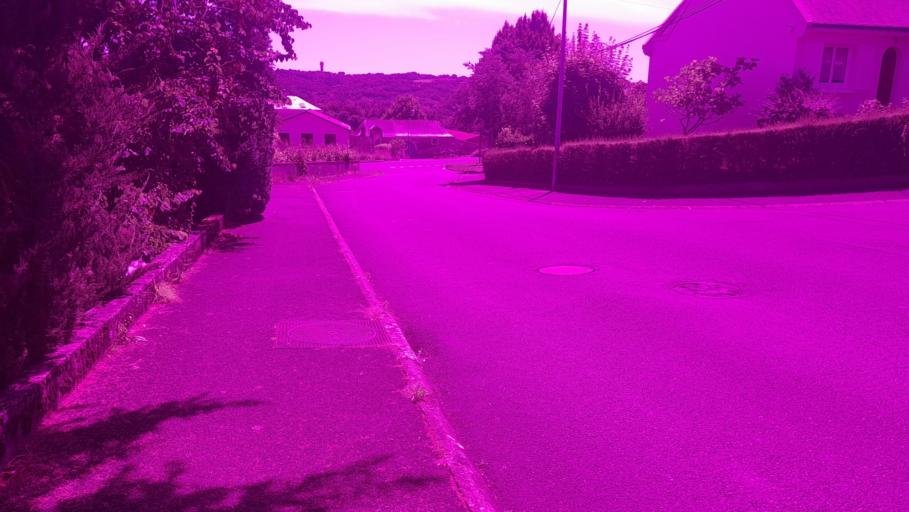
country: FR
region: Pays de la Loire
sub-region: Departement de la Loire-Atlantique
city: Oudon
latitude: 47.3496
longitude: -1.2811
